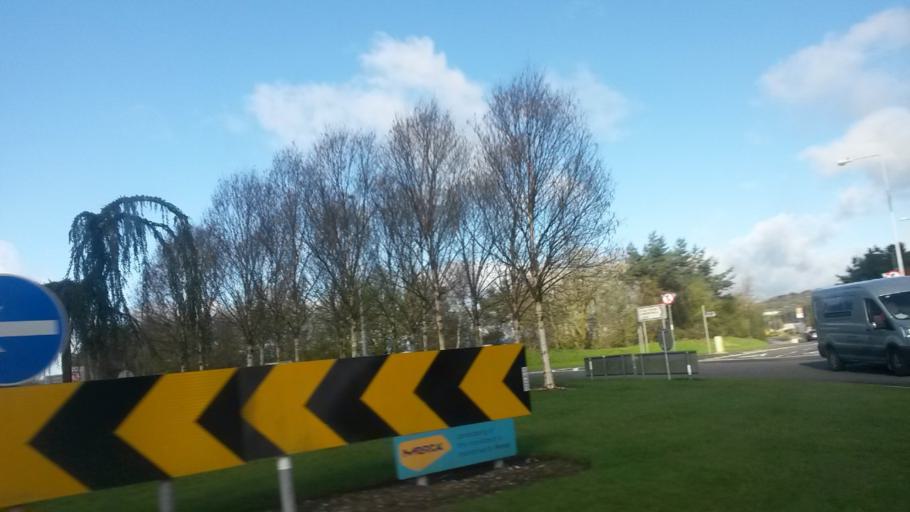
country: IE
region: Munster
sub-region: County Cork
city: Carrigtwohill
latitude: 51.9071
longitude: -8.2828
